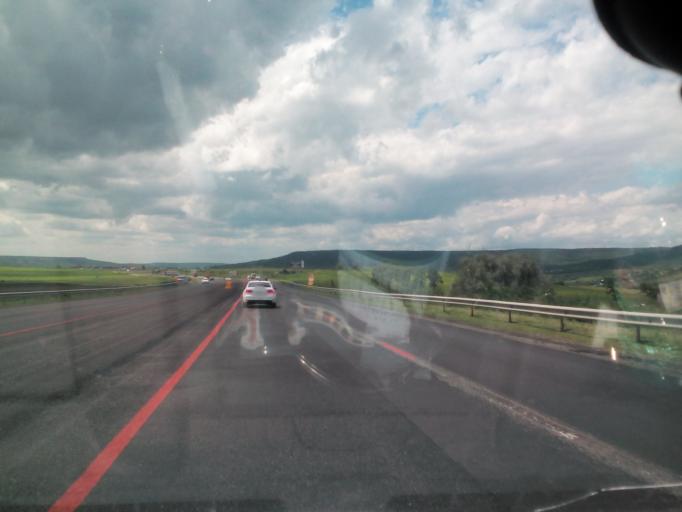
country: RU
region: Stavropol'skiy
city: Tatarka
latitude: 44.9514
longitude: 41.9413
